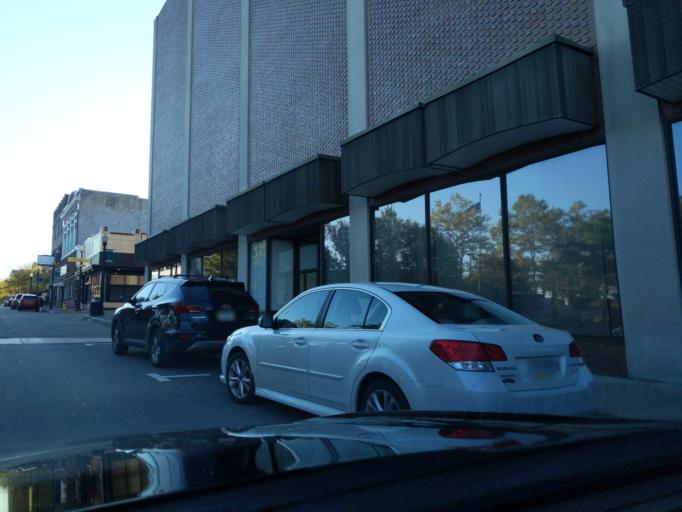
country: US
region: Pennsylvania
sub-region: Blair County
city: Altoona
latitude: 40.5145
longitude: -78.4030
